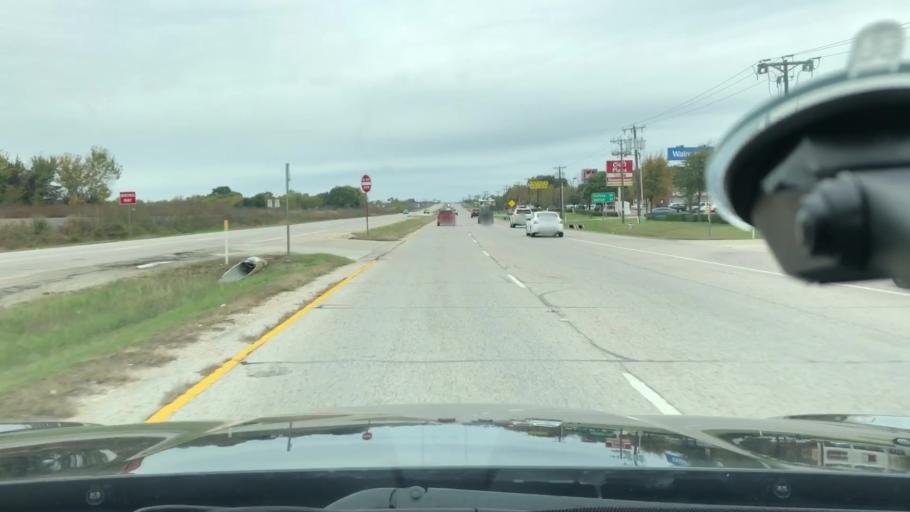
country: US
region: Texas
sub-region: Kaufman County
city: Terrell
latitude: 32.7371
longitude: -96.3044
